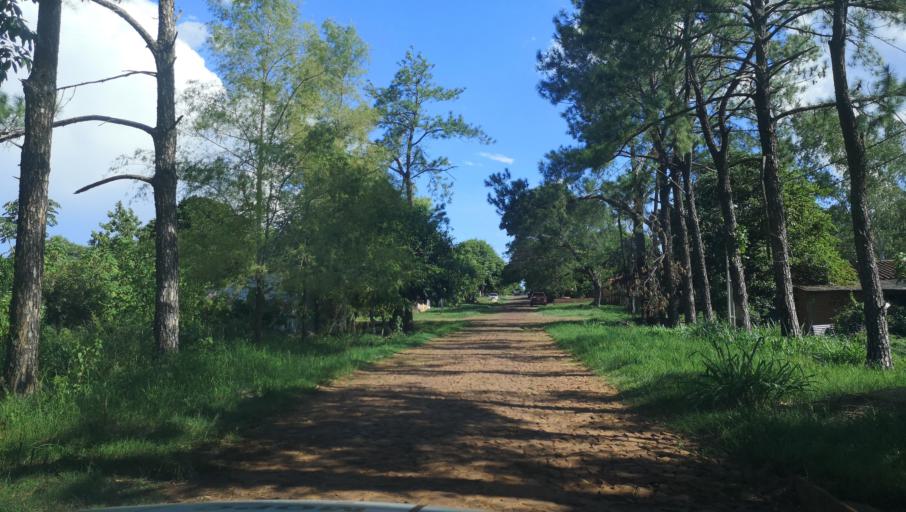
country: PY
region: Misiones
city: Santa Maria
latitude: -26.8833
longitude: -57.0192
